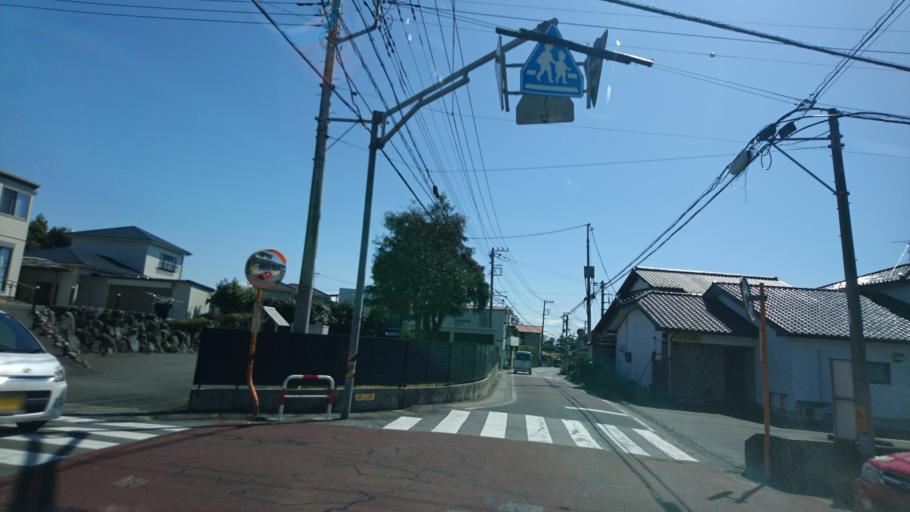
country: JP
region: Shizuoka
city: Fujinomiya
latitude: 35.2207
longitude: 138.6334
